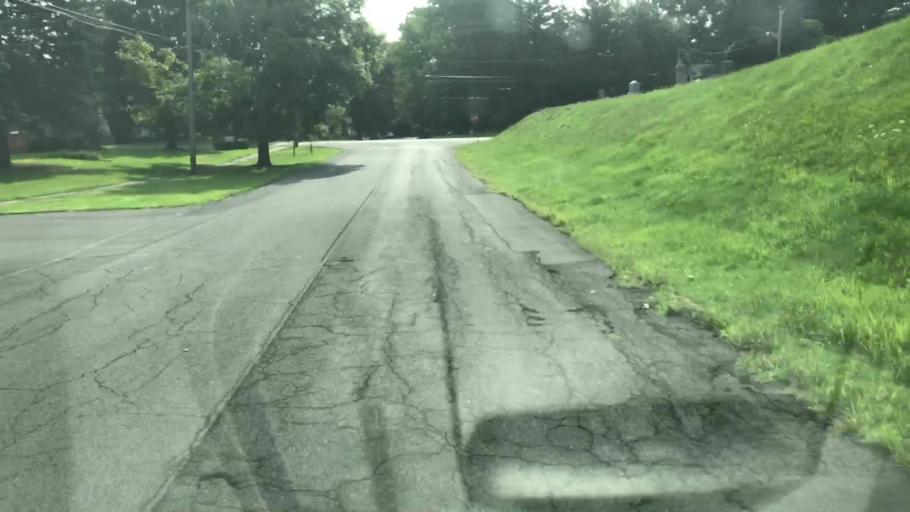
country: US
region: New York
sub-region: Onondaga County
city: Liverpool
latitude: 43.1100
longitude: -76.2072
